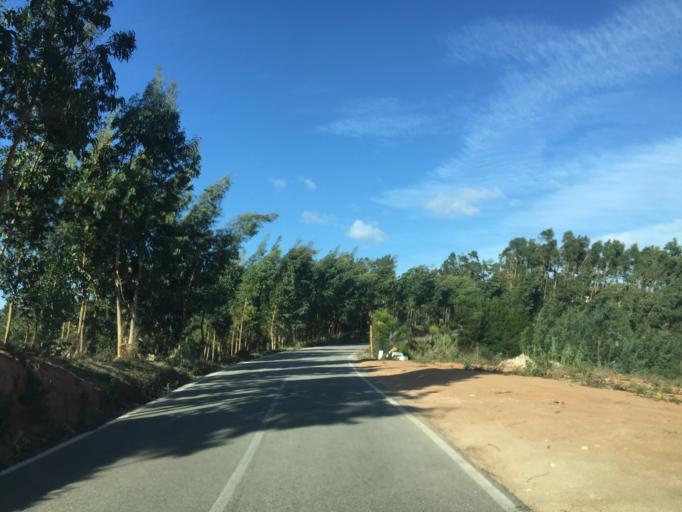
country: PT
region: Coimbra
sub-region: Figueira da Foz
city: Tavarede
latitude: 40.1762
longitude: -8.8382
